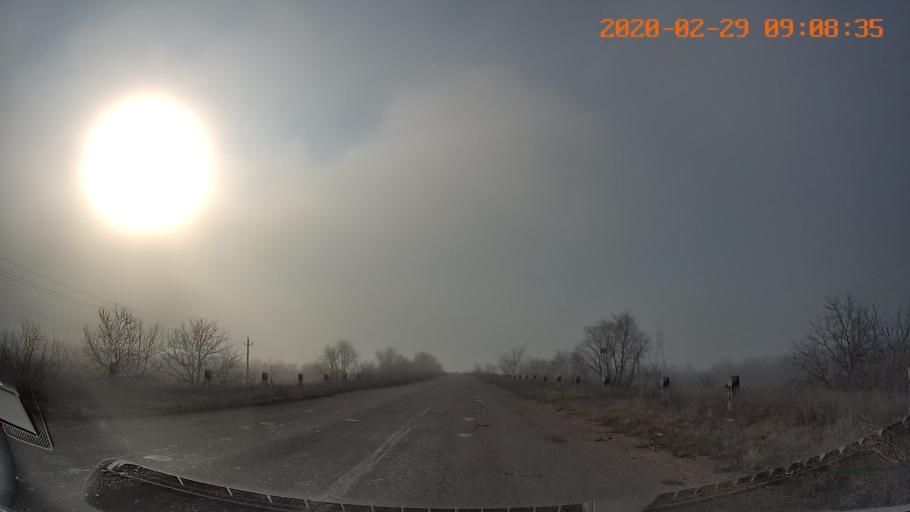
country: MD
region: Telenesti
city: Tiraspolul Nou
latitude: 46.8486
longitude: 29.7532
